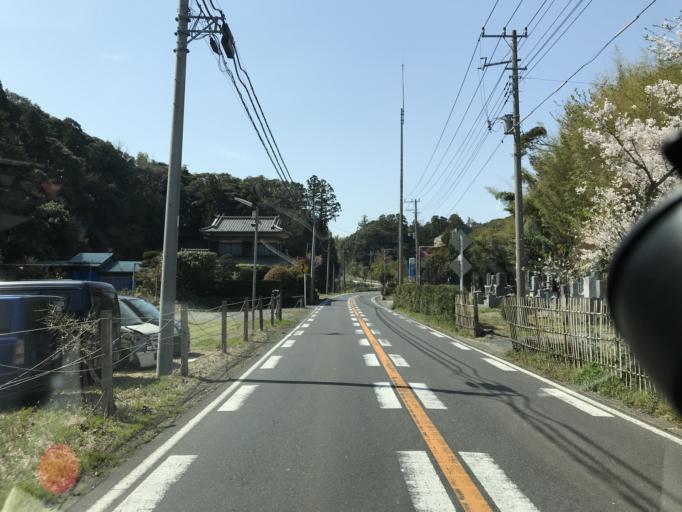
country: JP
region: Chiba
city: Yokaichiba
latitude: 35.7564
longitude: 140.5832
